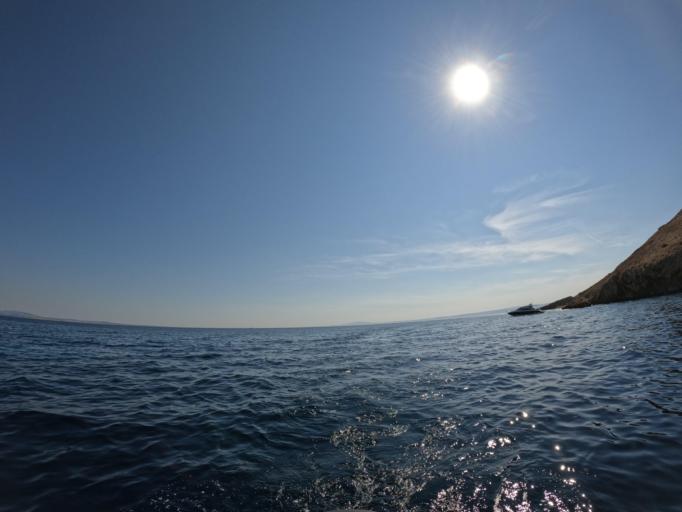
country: HR
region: Primorsko-Goranska
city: Punat
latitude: 44.9655
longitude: 14.6620
